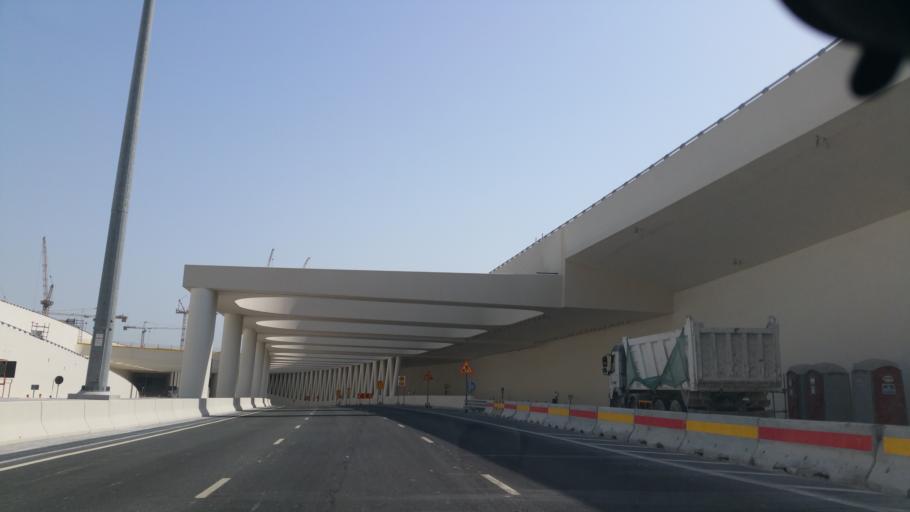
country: QA
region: Baladiyat Umm Salal
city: Umm Salal Muhammad
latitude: 25.4231
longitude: 51.5066
